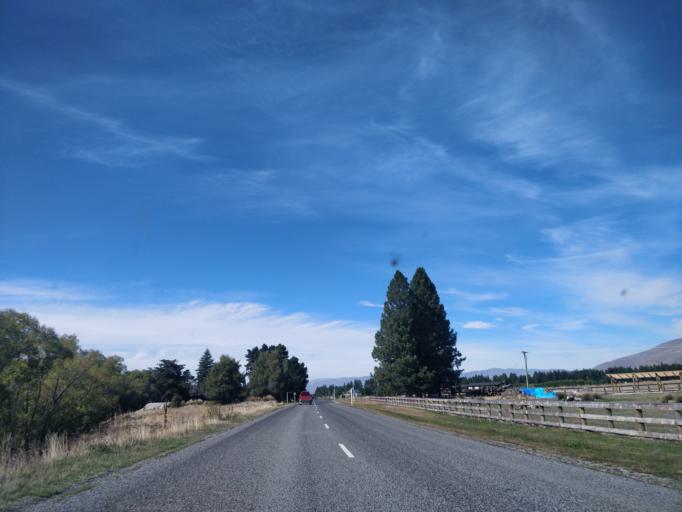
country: NZ
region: Otago
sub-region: Queenstown-Lakes District
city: Wanaka
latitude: -44.2389
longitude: 170.0804
